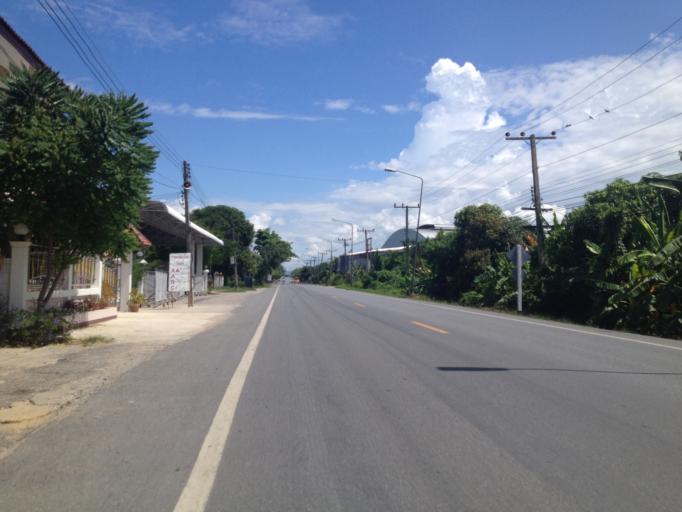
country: TH
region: Lamphun
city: Lamphun
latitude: 18.6024
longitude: 98.9609
